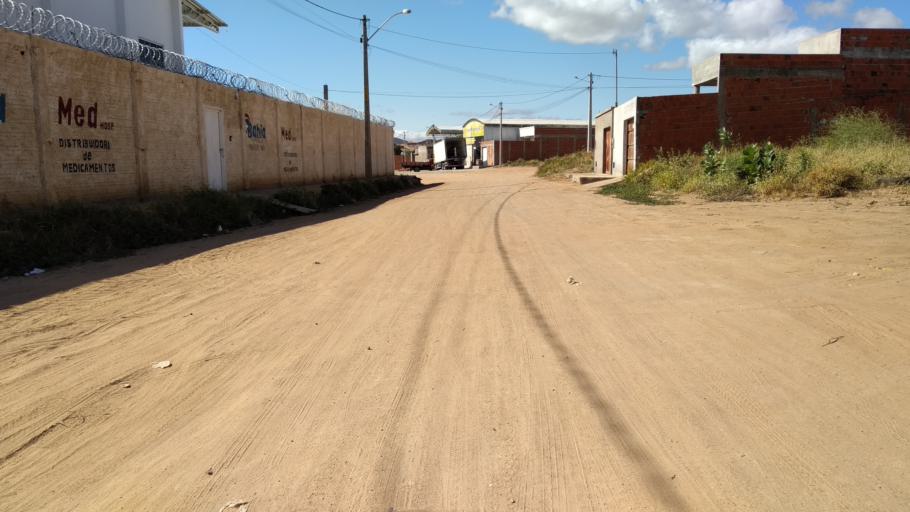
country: BR
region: Bahia
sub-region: Guanambi
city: Guanambi
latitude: -14.2398
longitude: -42.7700
